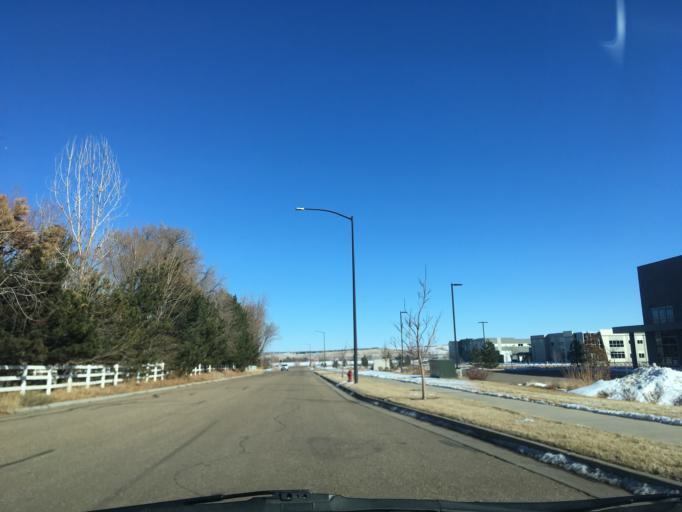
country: US
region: Colorado
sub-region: Boulder County
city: Louisville
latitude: 39.9628
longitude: -105.1141
